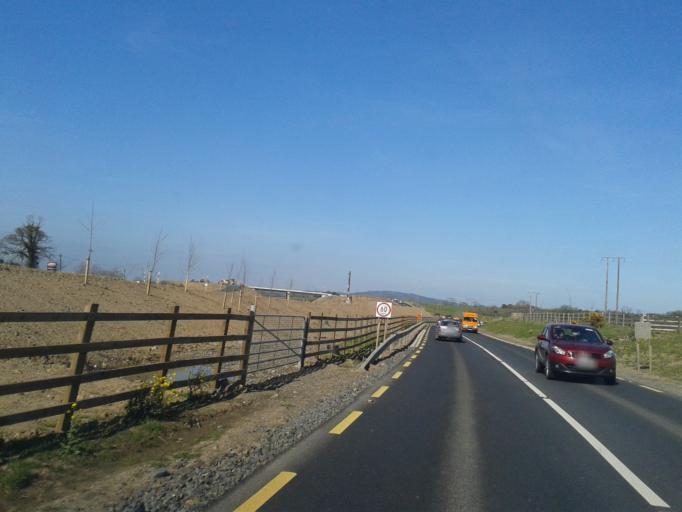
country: IE
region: Leinster
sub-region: Wicklow
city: Arklow
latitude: 52.8525
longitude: -6.1064
